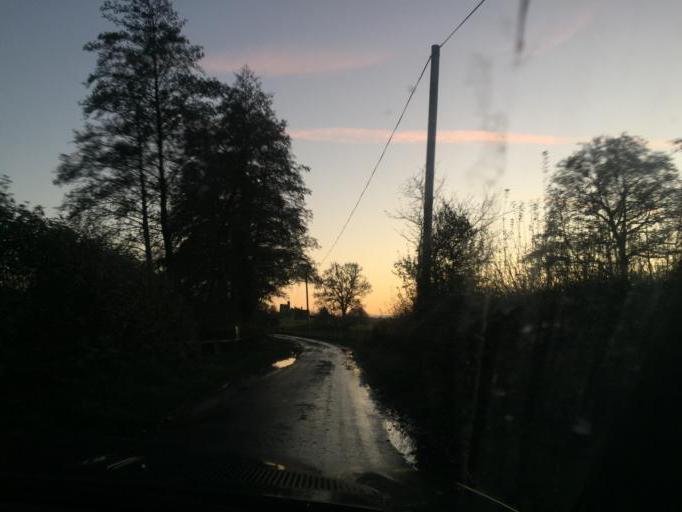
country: GB
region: England
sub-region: Northamptonshire
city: Brackley
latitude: 52.0954
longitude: -1.1114
